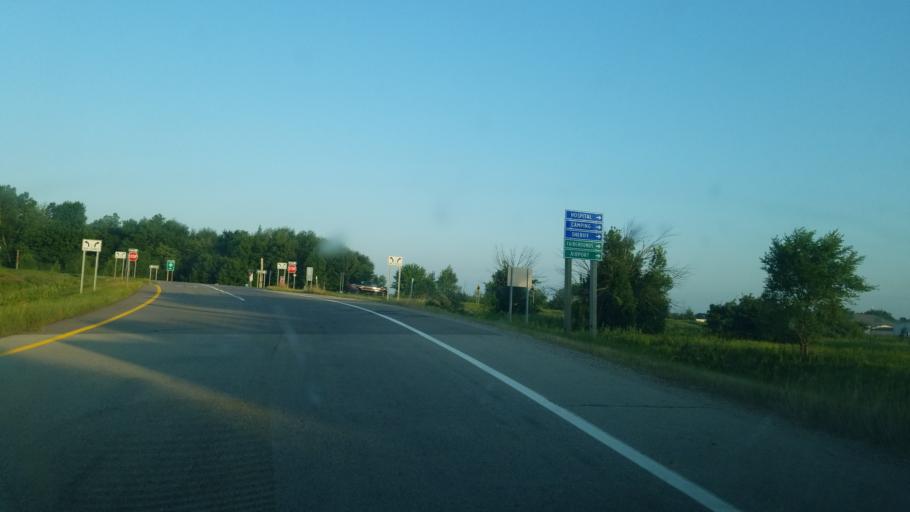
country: US
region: Michigan
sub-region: Ionia County
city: Ionia
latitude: 42.8808
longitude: -85.0737
